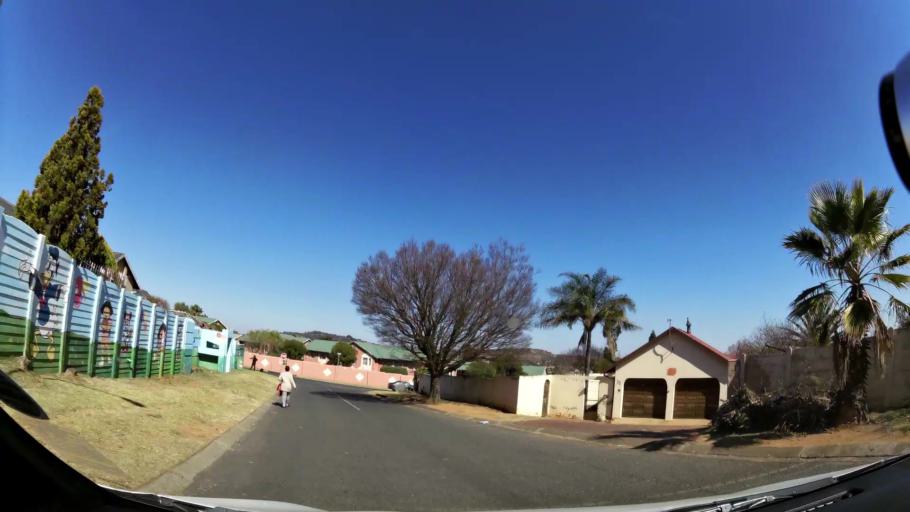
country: ZA
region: Gauteng
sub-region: City of Johannesburg Metropolitan Municipality
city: Johannesburg
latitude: -26.2634
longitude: 27.9928
